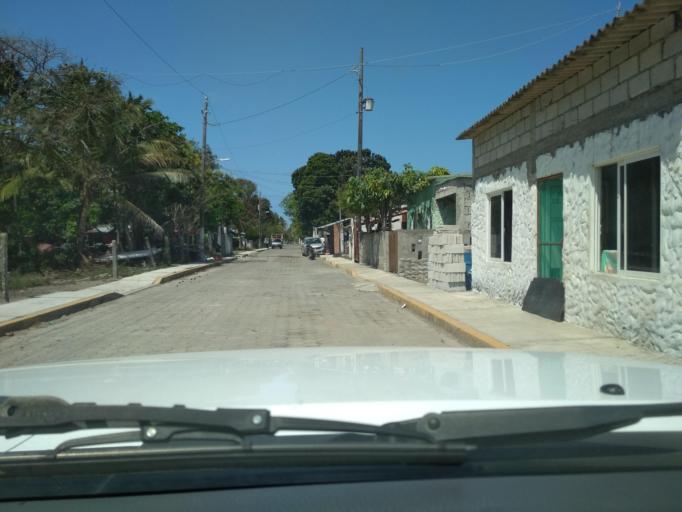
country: MX
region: Veracruz
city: Anton Lizardo
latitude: 19.0116
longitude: -95.9674
